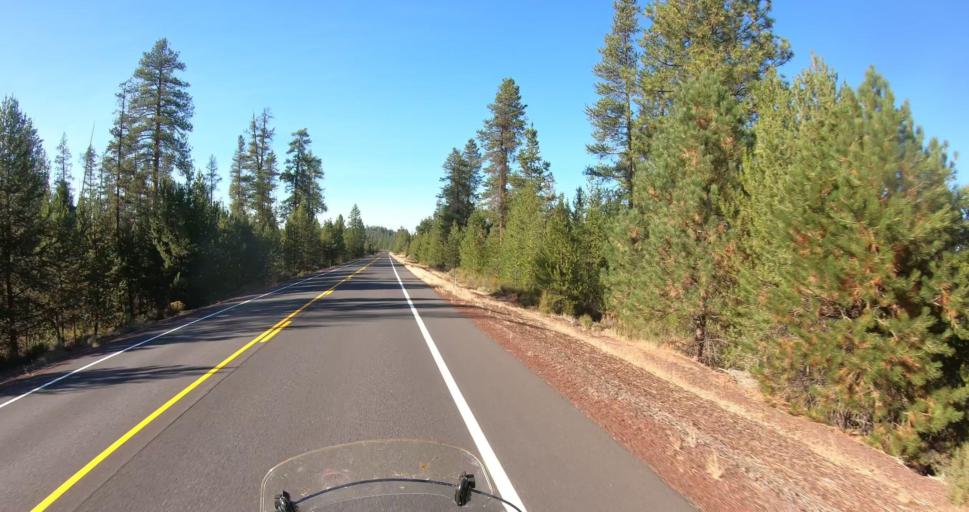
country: US
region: Oregon
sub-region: Deschutes County
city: La Pine
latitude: 43.4600
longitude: -121.3815
